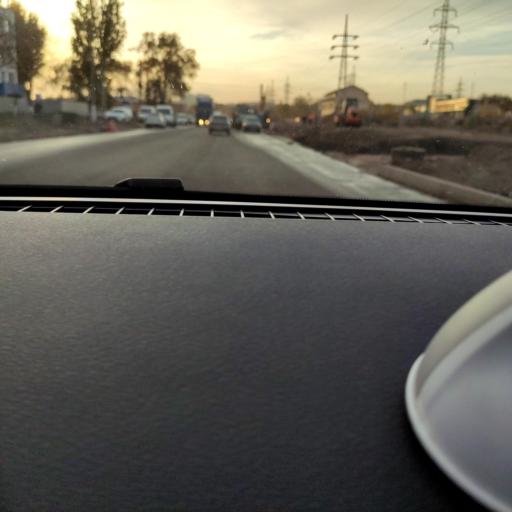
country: RU
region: Samara
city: Samara
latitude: 53.1949
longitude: 50.2386
